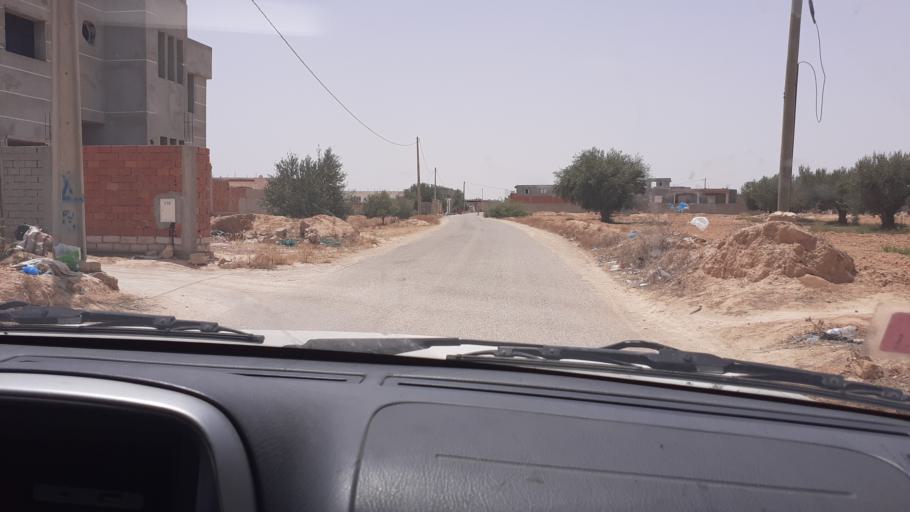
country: TN
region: Qabis
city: Matmata
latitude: 33.6091
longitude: 10.2870
